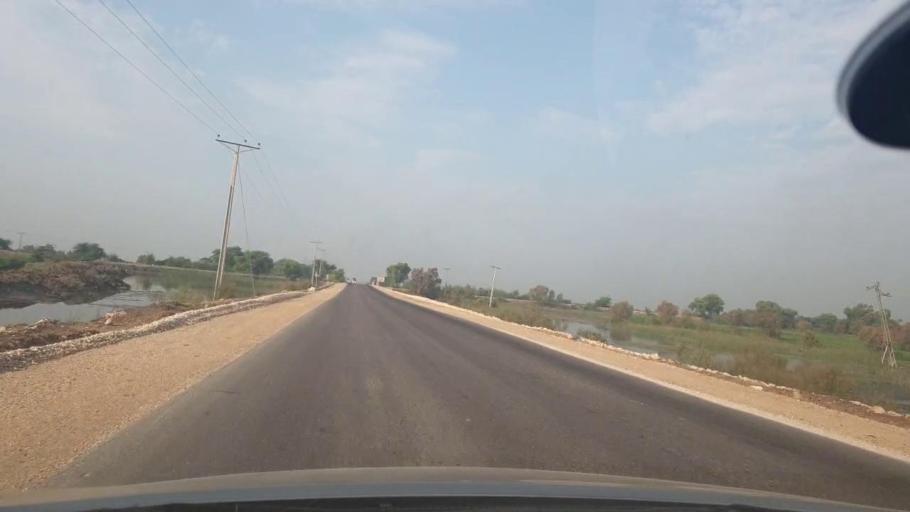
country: PK
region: Sindh
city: Jacobabad
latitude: 28.2364
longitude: 68.3897
